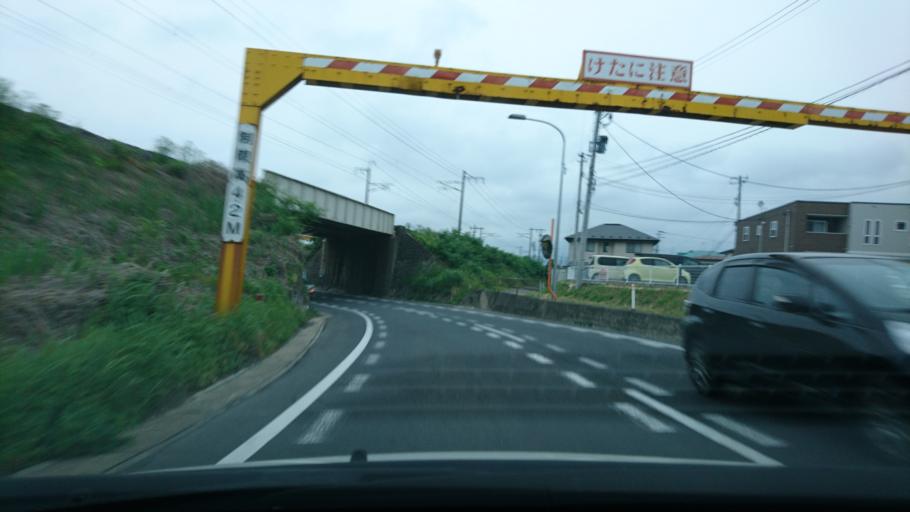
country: JP
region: Iwate
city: Ichinoseki
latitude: 38.9132
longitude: 141.1316
